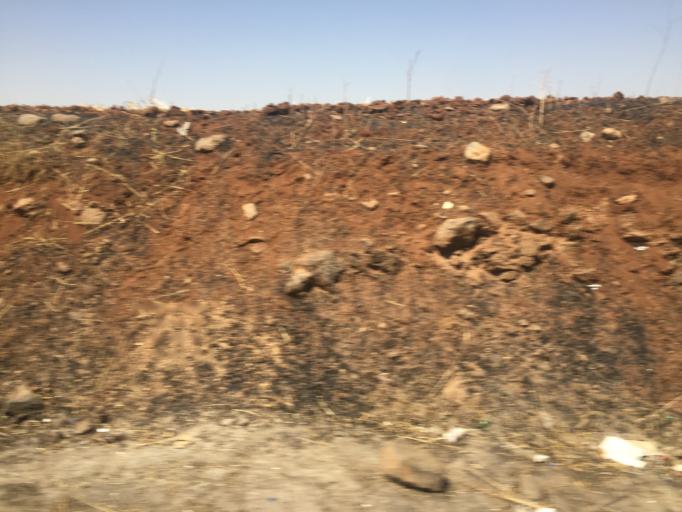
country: TR
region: Diyarbakir
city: Diyarbakir
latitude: 37.8730
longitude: 40.2187
